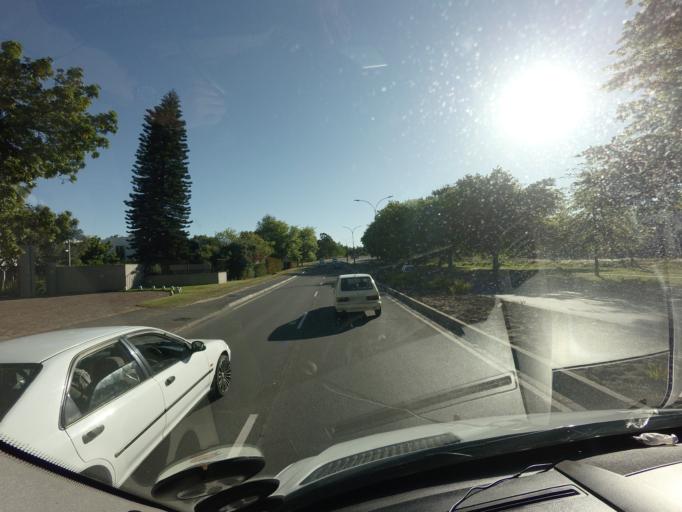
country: ZA
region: Western Cape
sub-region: Cape Winelands District Municipality
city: Stellenbosch
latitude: -33.9410
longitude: 18.8478
